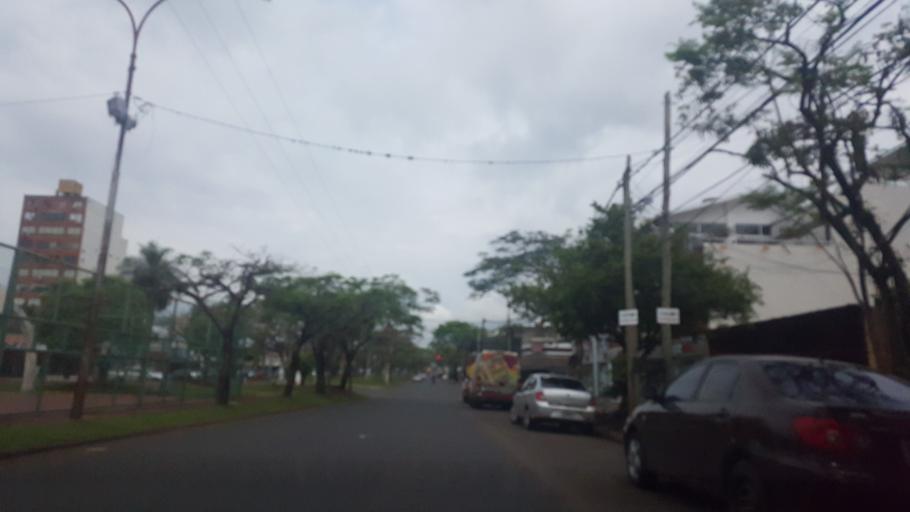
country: AR
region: Misiones
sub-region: Departamento de Capital
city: Posadas
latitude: -27.3655
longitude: -55.9012
